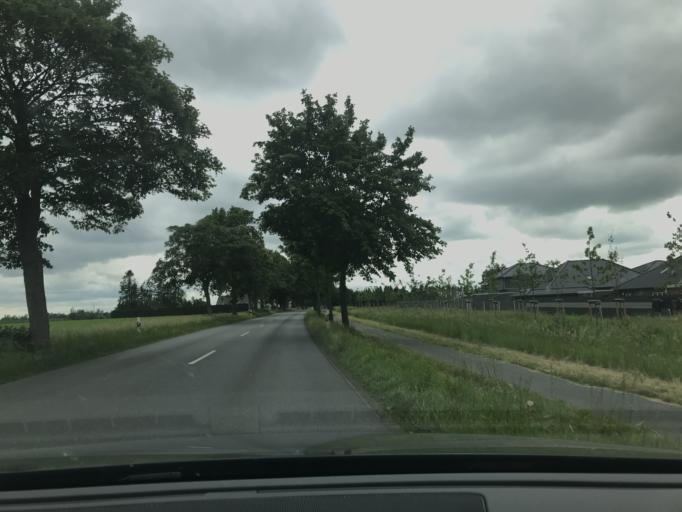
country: DE
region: Lower Saxony
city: Loxstedt
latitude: 53.4644
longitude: 8.6389
